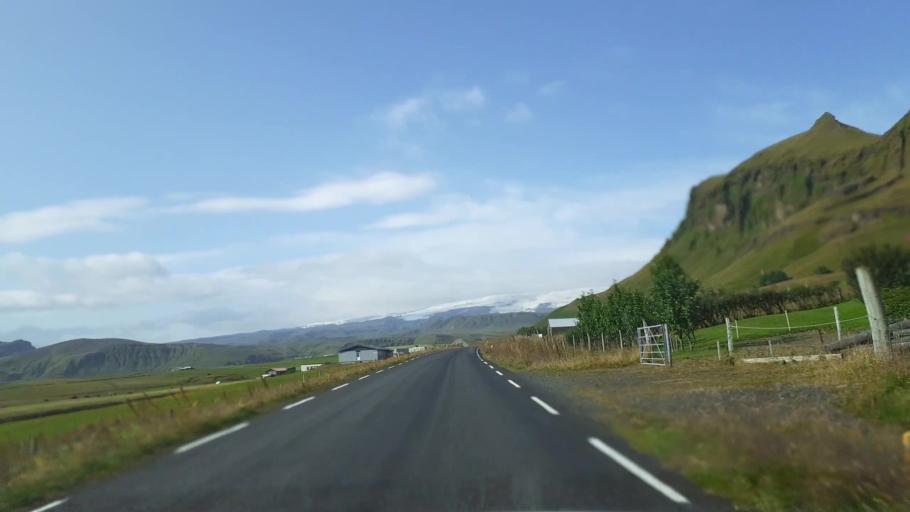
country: IS
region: South
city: Vestmannaeyjar
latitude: 63.4219
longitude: -19.0490
